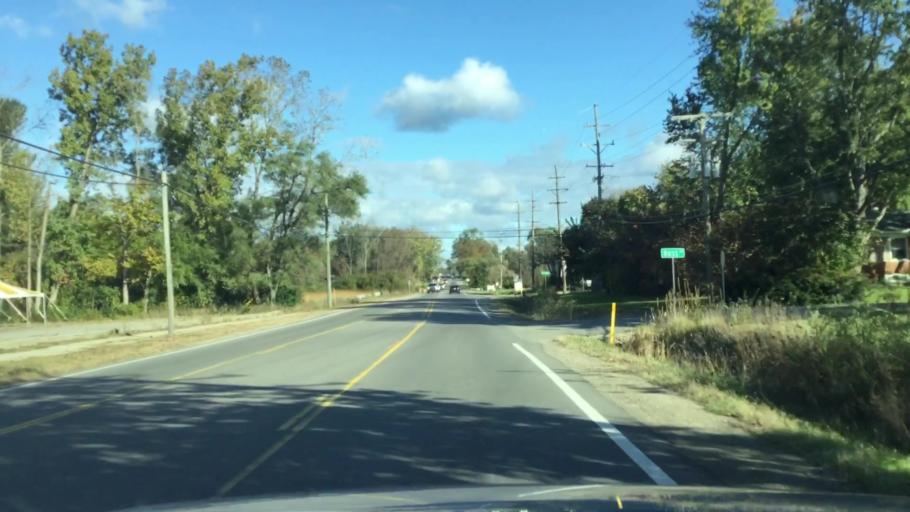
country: US
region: Michigan
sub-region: Oakland County
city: Waterford
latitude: 42.6623
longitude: -83.3863
